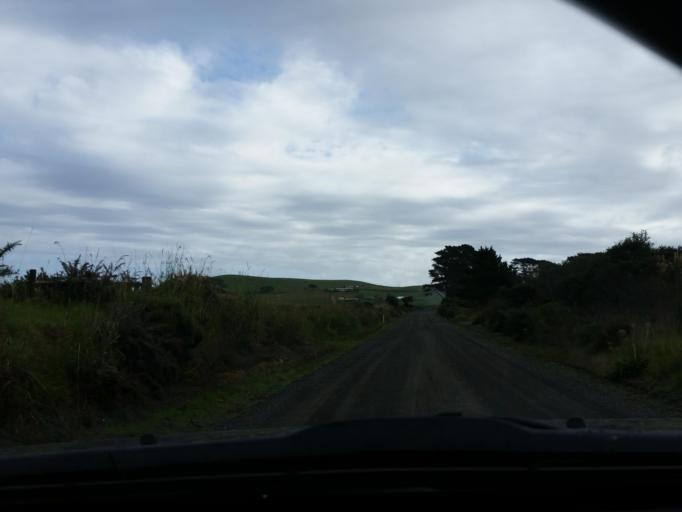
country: NZ
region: Northland
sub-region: Kaipara District
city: Dargaville
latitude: -36.0355
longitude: 173.8598
